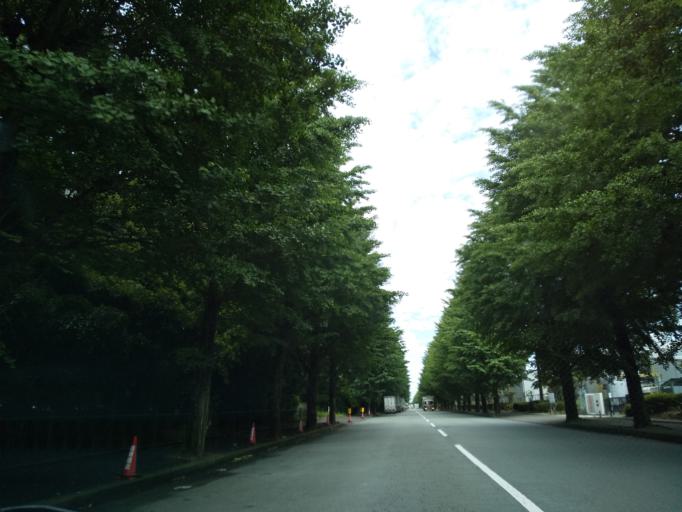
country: JP
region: Kanagawa
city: Zama
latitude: 35.5143
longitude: 139.3488
